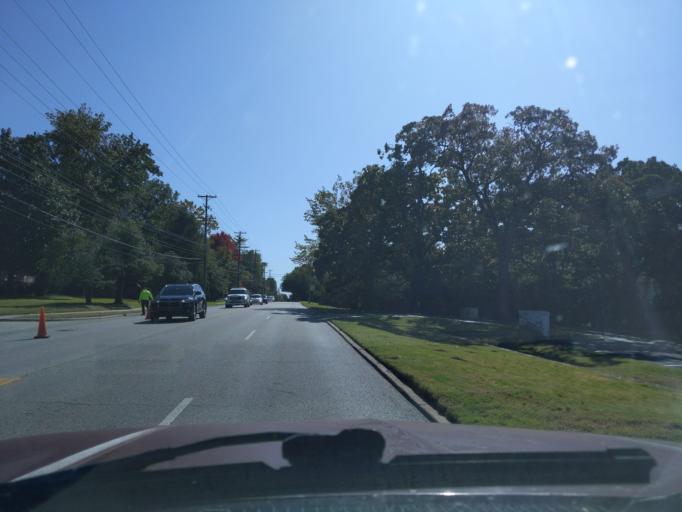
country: US
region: Oklahoma
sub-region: Tulsa County
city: Tulsa
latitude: 36.1107
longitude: -95.9581
